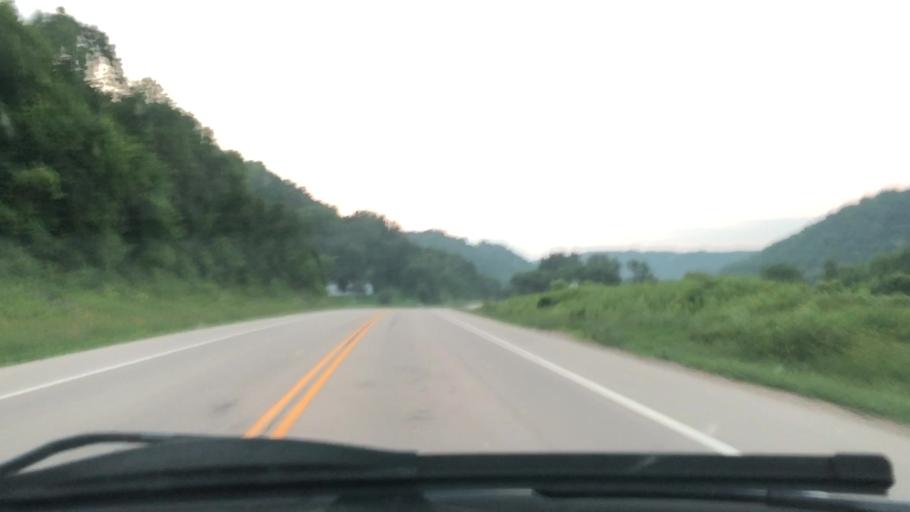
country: US
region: Wisconsin
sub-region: Richland County
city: Richland Center
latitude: 43.3566
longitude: -90.5557
